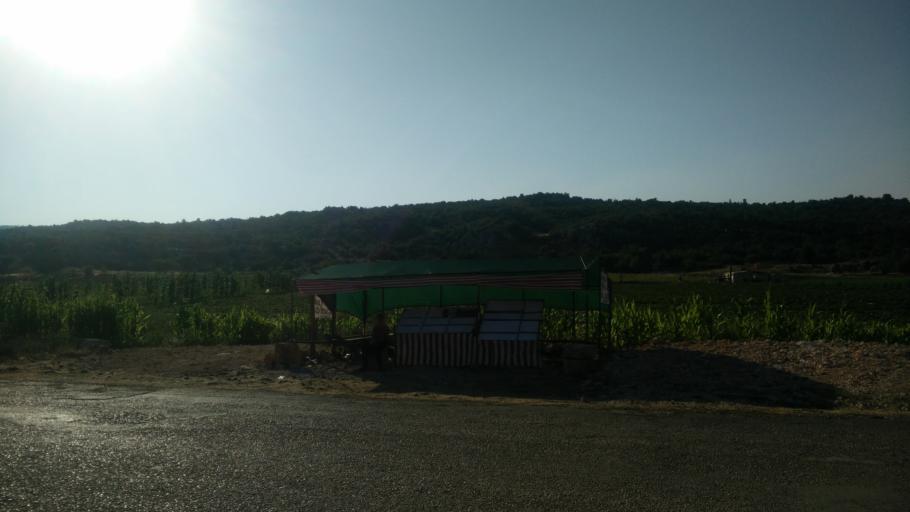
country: TR
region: Mersin
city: Kirobasi
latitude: 36.5868
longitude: 33.9685
